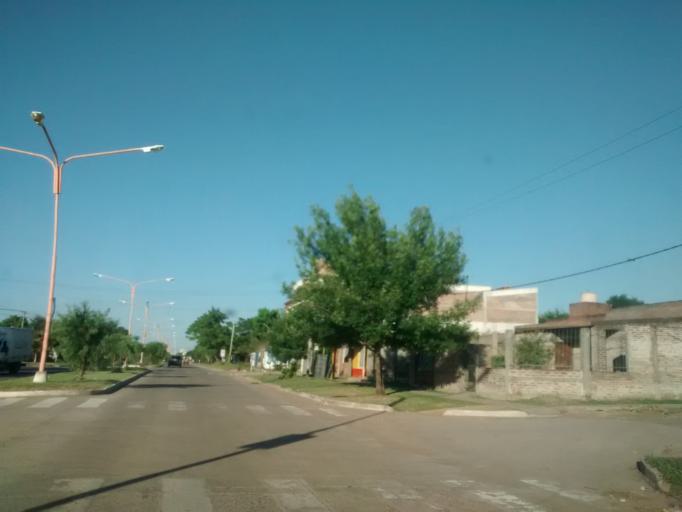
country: AR
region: Chaco
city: Resistencia
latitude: -27.4646
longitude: -59.0102
